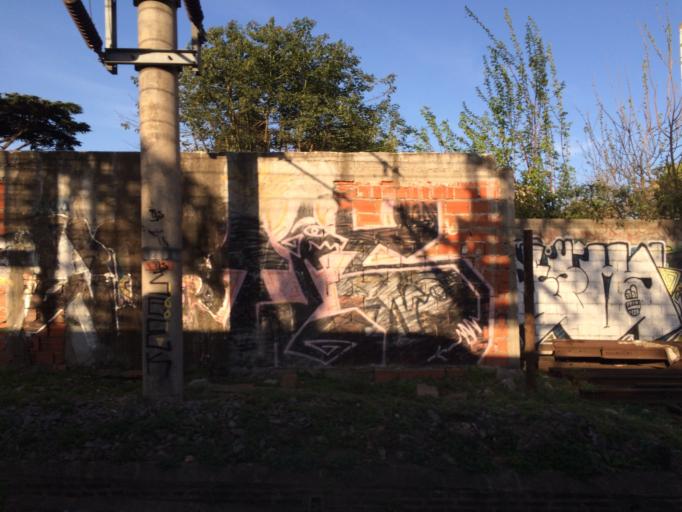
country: AR
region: Buenos Aires
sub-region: Partido de Lomas de Zamora
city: Lomas de Zamora
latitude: -34.7731
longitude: -58.3967
